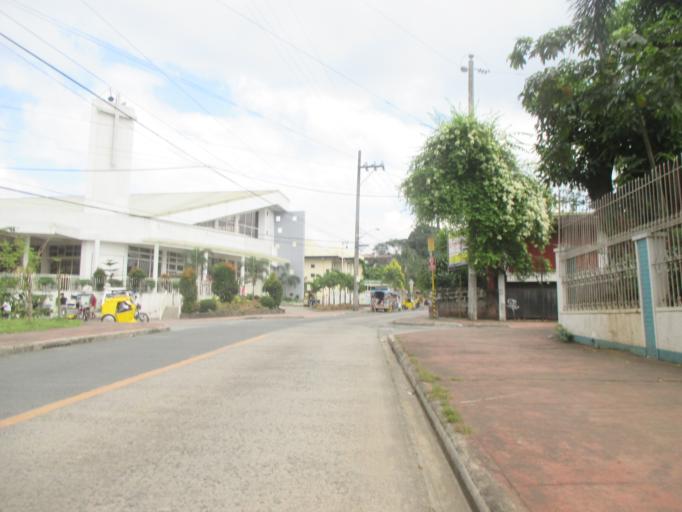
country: PH
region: Calabarzon
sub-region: Province of Rizal
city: Antipolo
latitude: 14.6530
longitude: 121.1184
